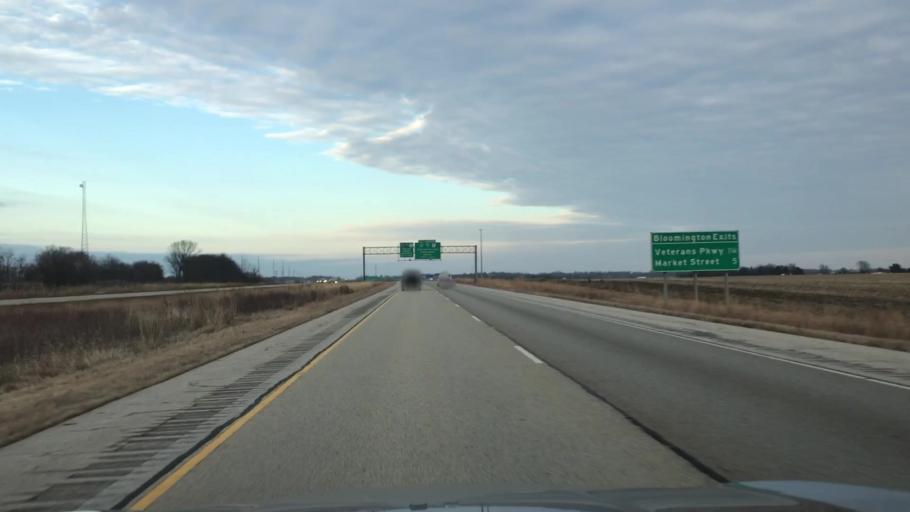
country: US
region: Illinois
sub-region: McLean County
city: Bloomington
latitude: 40.4239
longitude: -89.0409
